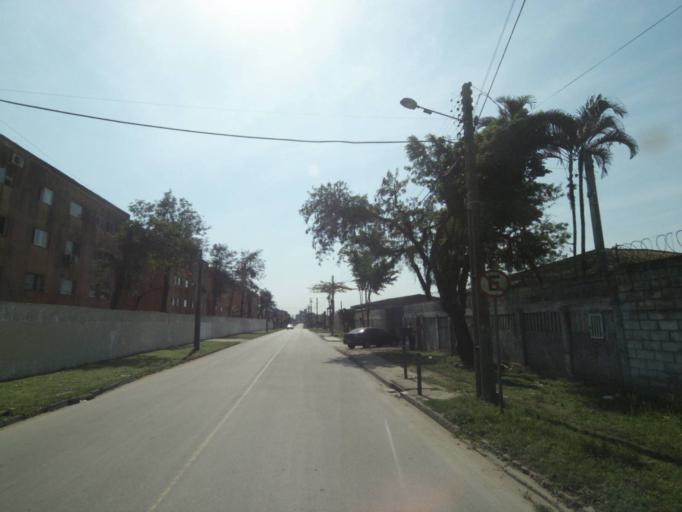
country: BR
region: Parana
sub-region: Paranagua
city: Paranagua
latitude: -25.5501
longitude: -48.5537
